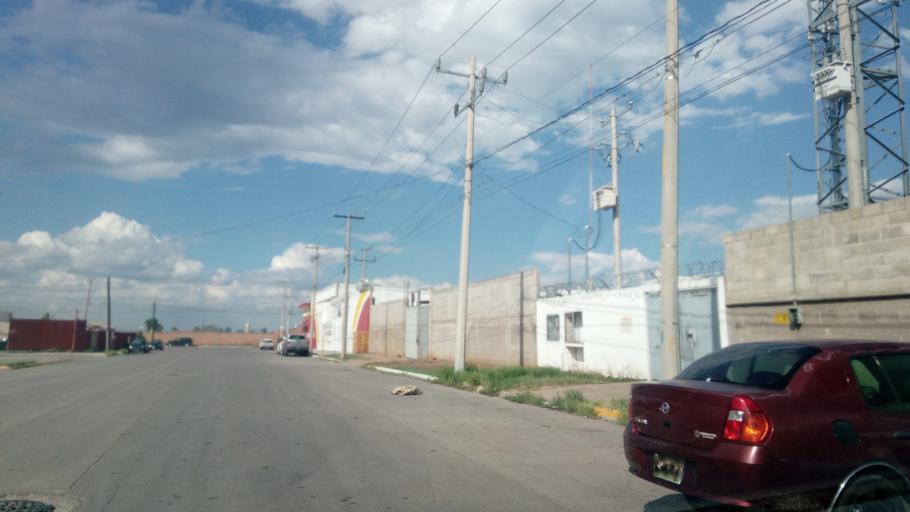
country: MX
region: Durango
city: Victoria de Durango
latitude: 24.0699
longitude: -104.6056
